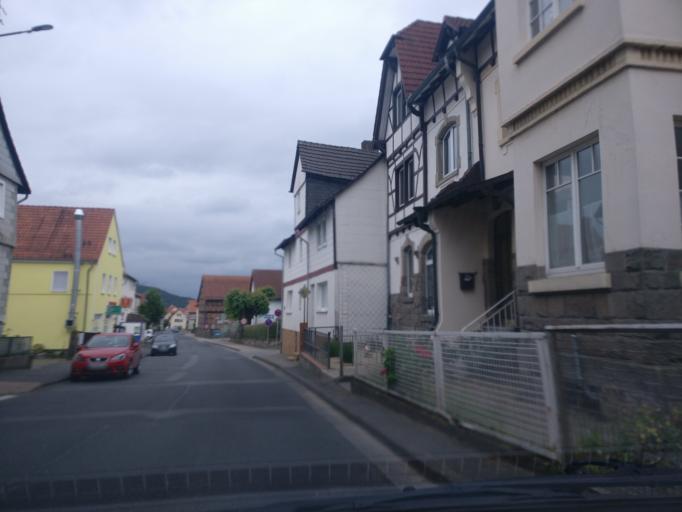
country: DE
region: Hesse
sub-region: Regierungsbezirk Kassel
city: Baunatal
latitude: 51.2735
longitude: 9.3741
